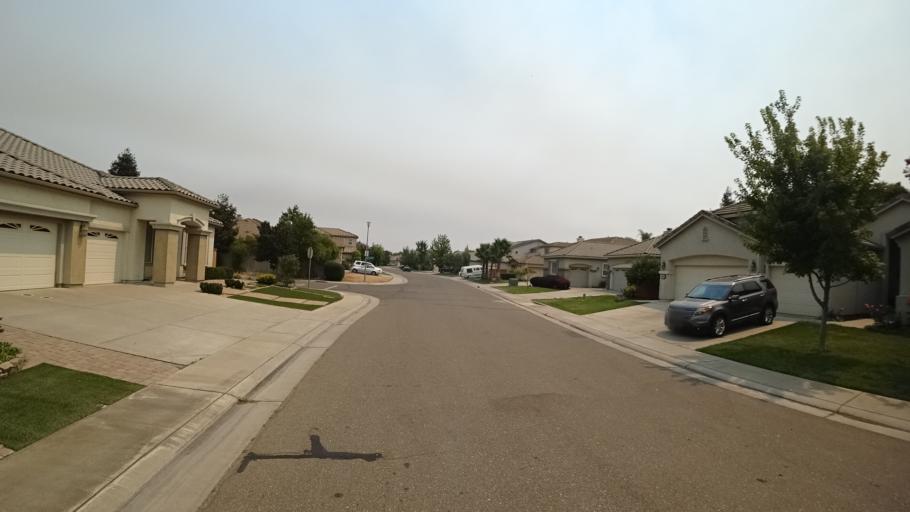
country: US
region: California
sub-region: Sacramento County
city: Laguna
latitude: 38.3992
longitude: -121.4221
